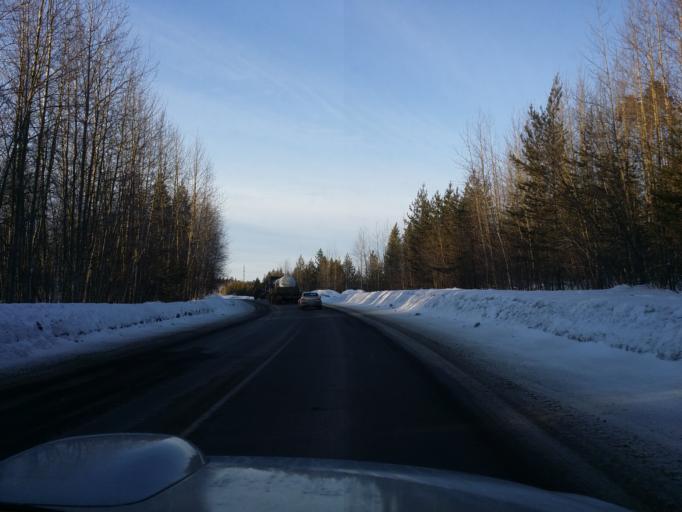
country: RU
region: Khanty-Mansiyskiy Avtonomnyy Okrug
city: Izluchinsk
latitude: 60.9602
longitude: 76.8512
